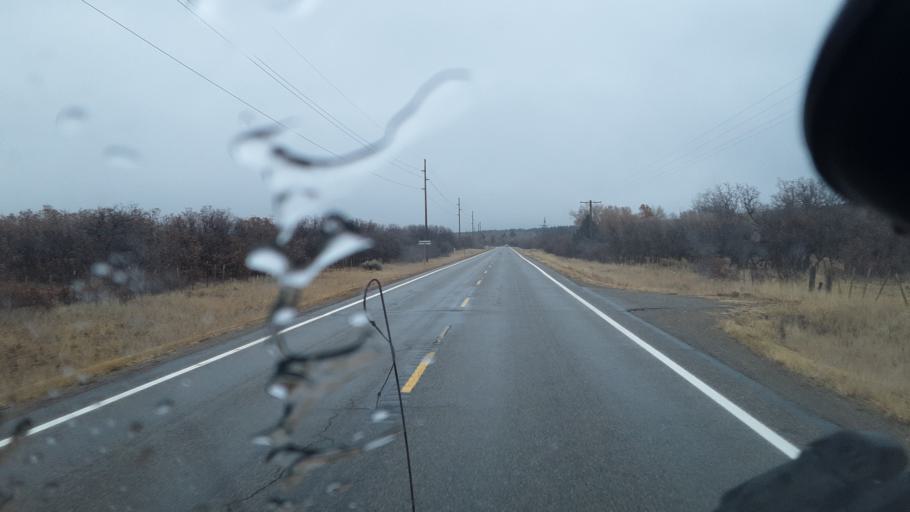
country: US
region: Colorado
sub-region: La Plata County
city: Durango
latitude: 37.2358
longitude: -108.0437
